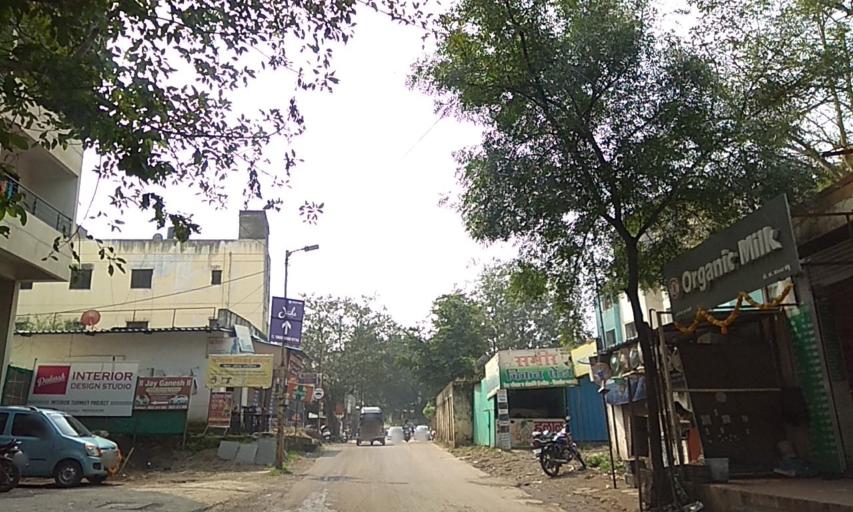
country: IN
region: Maharashtra
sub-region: Pune Division
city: Pimpri
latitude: 18.5612
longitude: 73.7864
